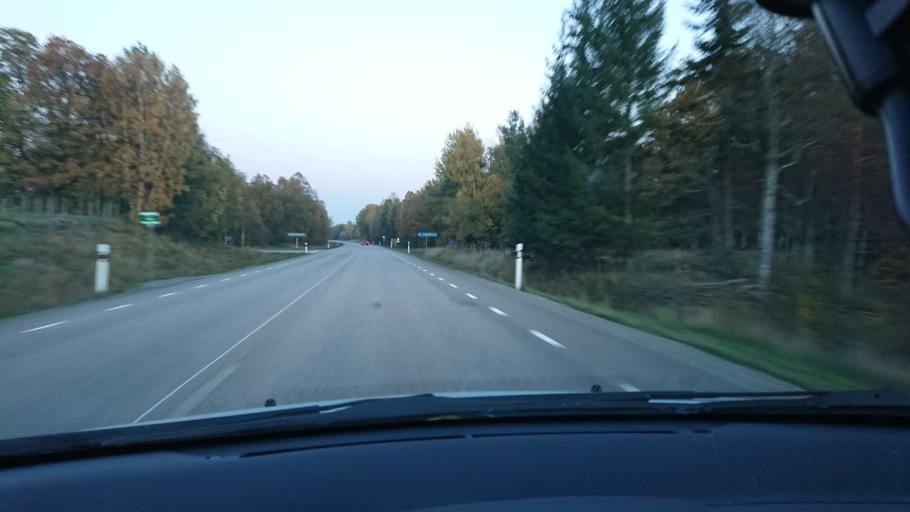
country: SE
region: Kronoberg
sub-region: Markaryds Kommun
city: Stromsnasbruk
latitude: 56.7555
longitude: 13.7229
